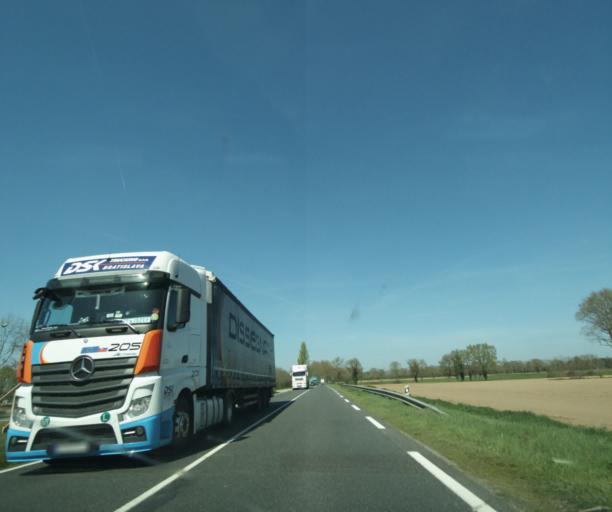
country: FR
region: Bourgogne
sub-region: Departement de la Nievre
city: Chantenay-Saint-Imbert
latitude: 46.6834
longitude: 3.2243
